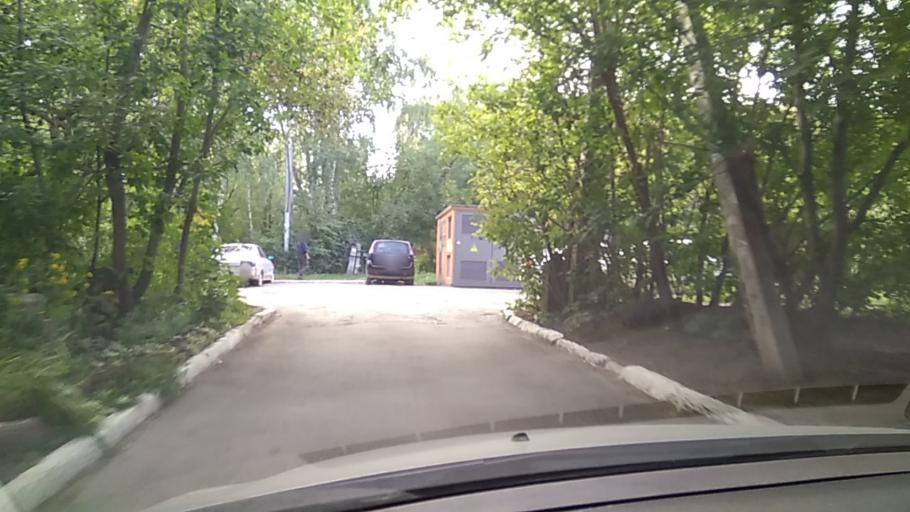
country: RU
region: Sverdlovsk
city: Yekaterinburg
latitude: 56.8833
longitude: 60.5709
